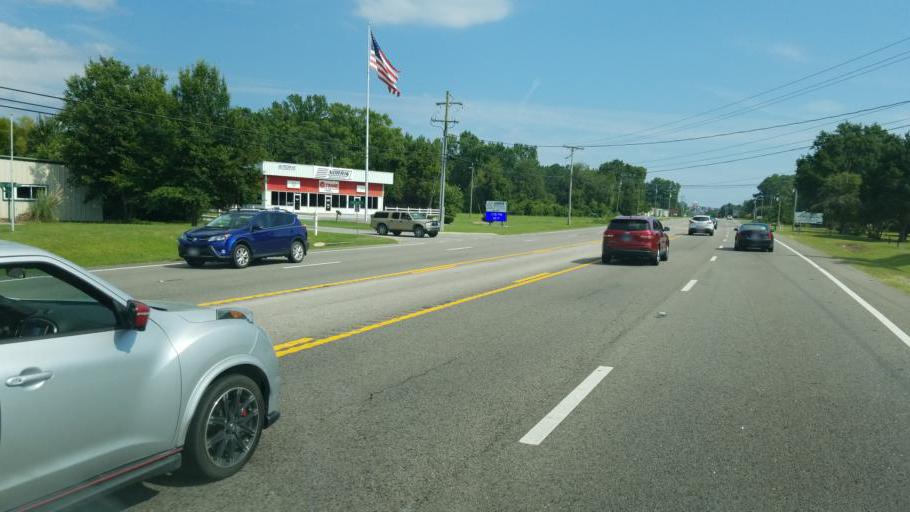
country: US
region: North Carolina
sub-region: Dare County
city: Southern Shores
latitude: 36.1251
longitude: -75.8357
